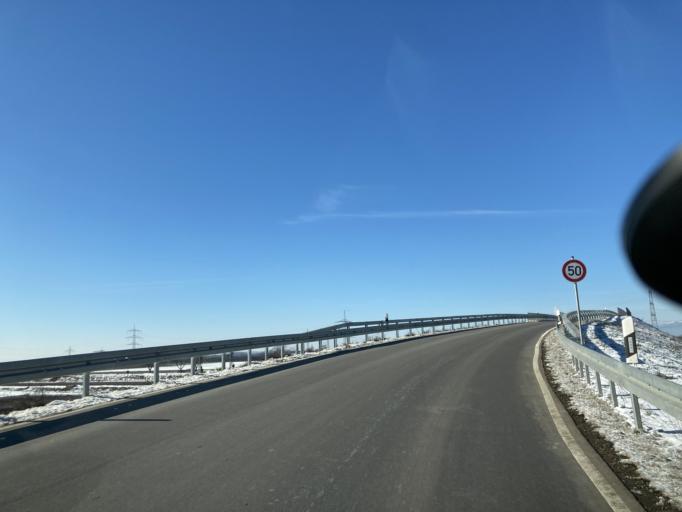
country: DE
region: Baden-Wuerttemberg
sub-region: Freiburg Region
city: Auggen
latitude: 47.7840
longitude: 7.5847
